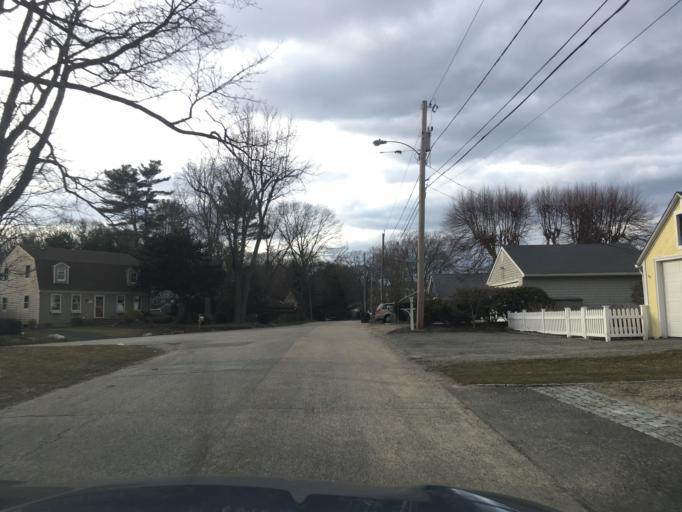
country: US
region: Rhode Island
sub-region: Kent County
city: Warwick
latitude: 41.6676
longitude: -71.4224
